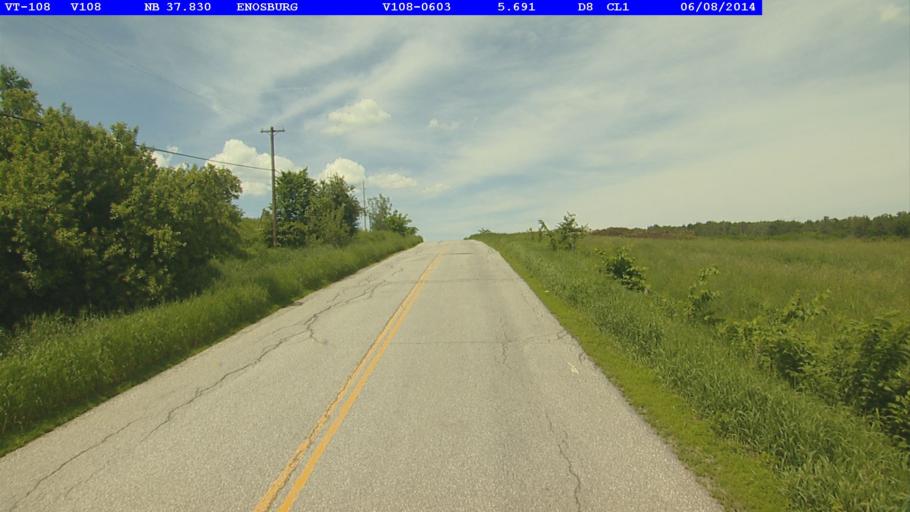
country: US
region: Vermont
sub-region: Franklin County
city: Enosburg Falls
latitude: 44.9221
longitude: -72.8080
